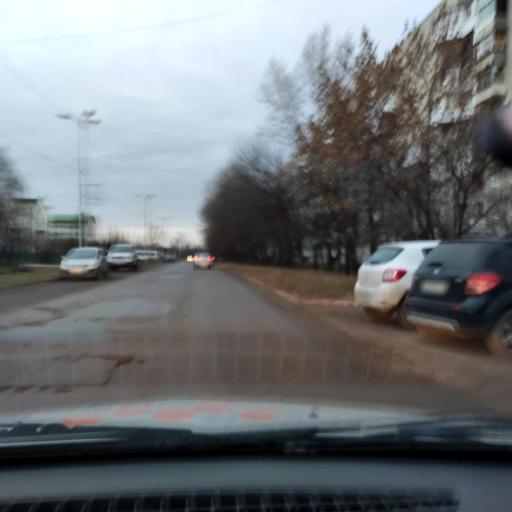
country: RU
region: Bashkortostan
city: Mikhaylovka
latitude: 54.7107
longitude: 55.8272
